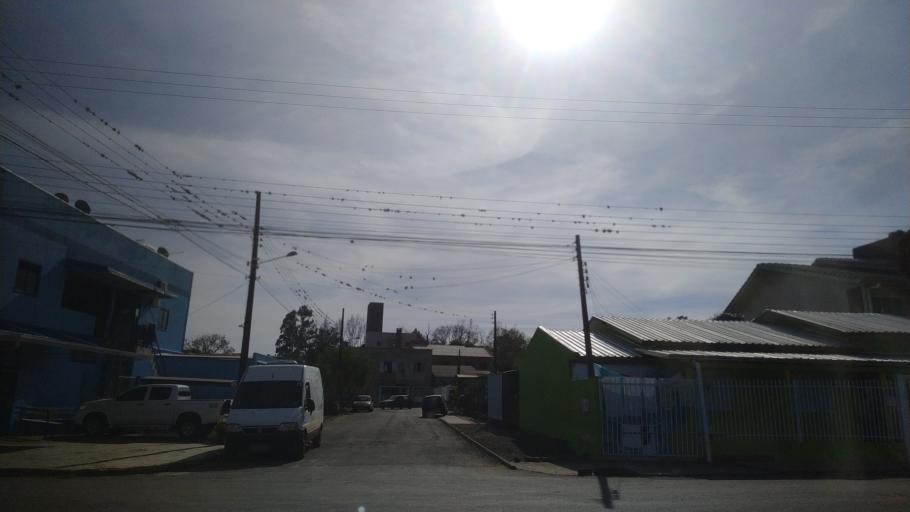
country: BR
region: Santa Catarina
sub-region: Chapeco
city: Chapeco
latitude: -27.1019
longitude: -52.6539
